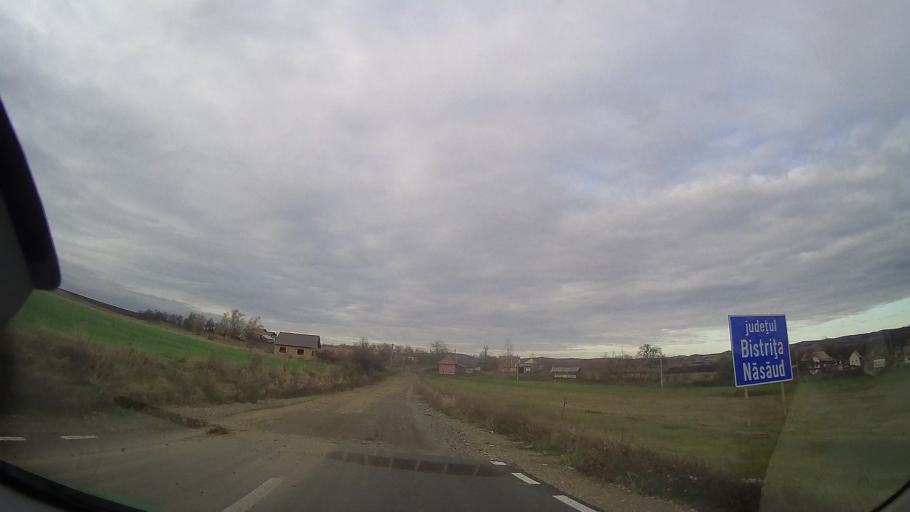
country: RO
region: Bistrita-Nasaud
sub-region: Comuna Milas
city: Milas
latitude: 46.8280
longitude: 24.4694
